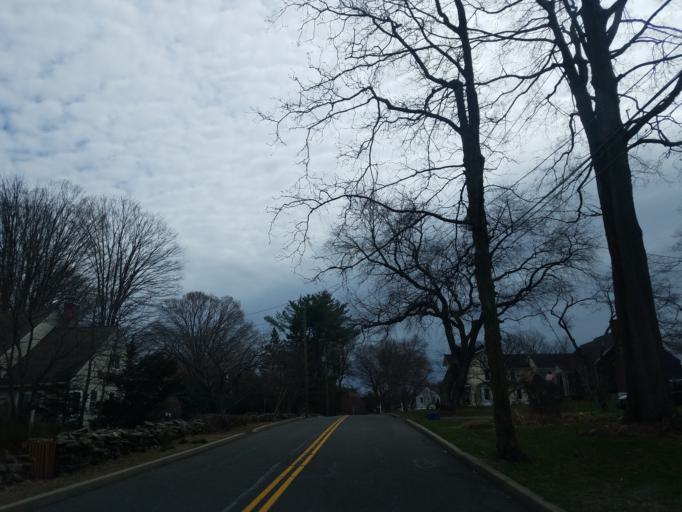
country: US
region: Connecticut
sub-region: Fairfield County
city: Bridgeport
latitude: 41.1911
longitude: -73.2425
